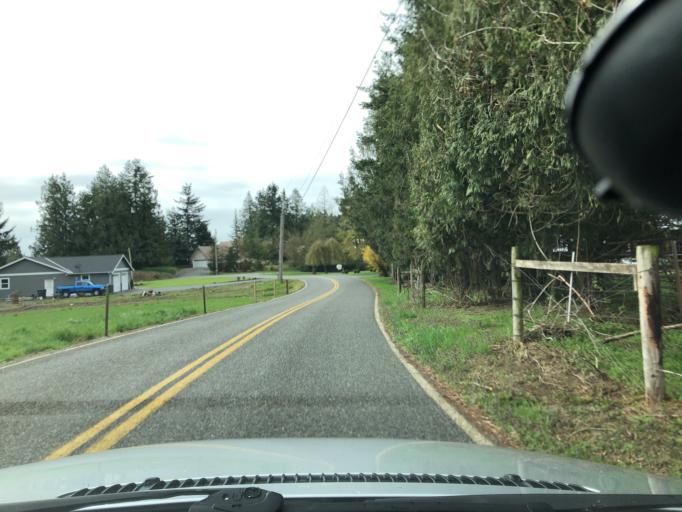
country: US
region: Washington
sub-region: Whatcom County
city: Lynden
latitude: 48.9842
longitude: -122.5186
